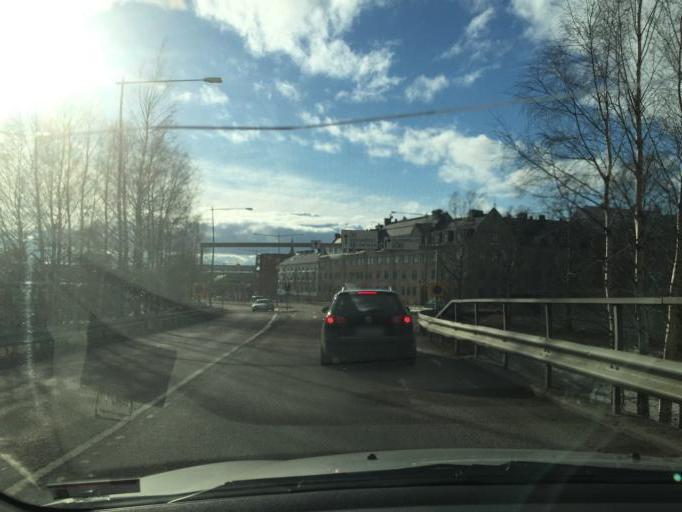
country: SE
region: Norrbotten
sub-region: Lulea Kommun
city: Lulea
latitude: 65.5822
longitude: 22.1663
